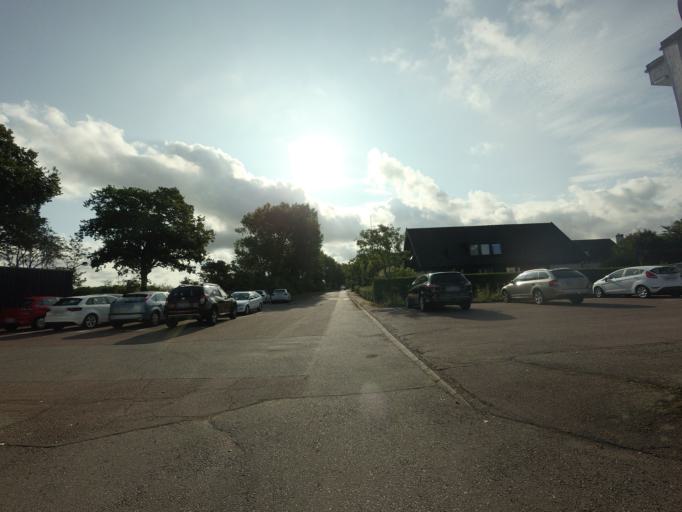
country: SE
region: Skane
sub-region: Hoganas Kommun
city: Hoganas
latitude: 56.1616
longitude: 12.5754
